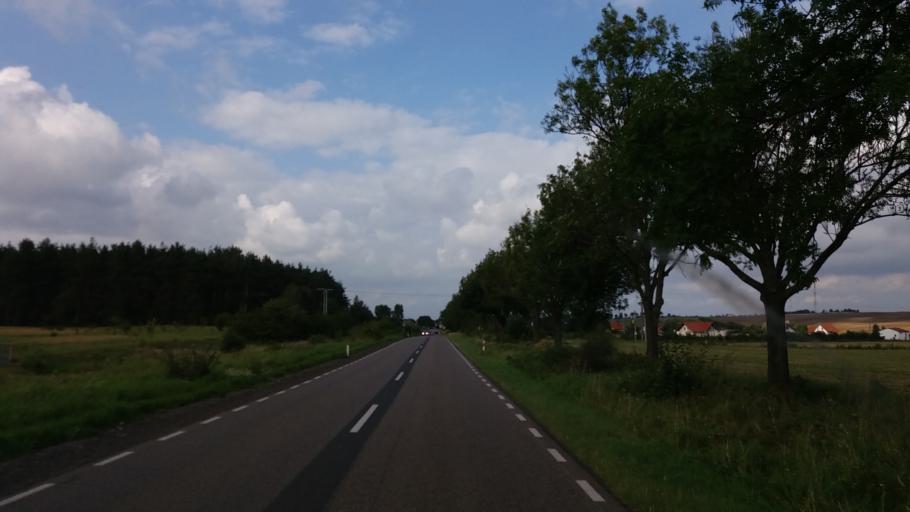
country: PL
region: West Pomeranian Voivodeship
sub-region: Powiat choszczenski
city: Pelczyce
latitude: 53.0266
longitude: 15.2902
